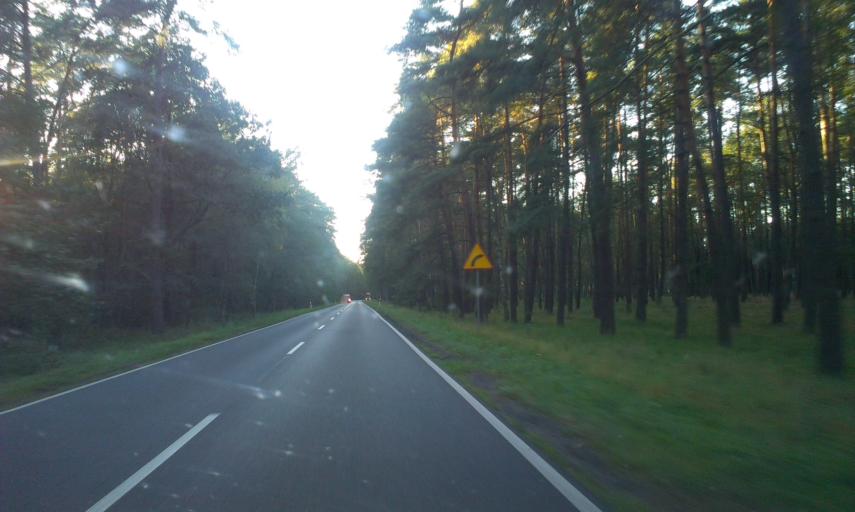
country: PL
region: Pomeranian Voivodeship
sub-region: Powiat czluchowski
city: Czarne
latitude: 53.7062
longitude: 16.8651
